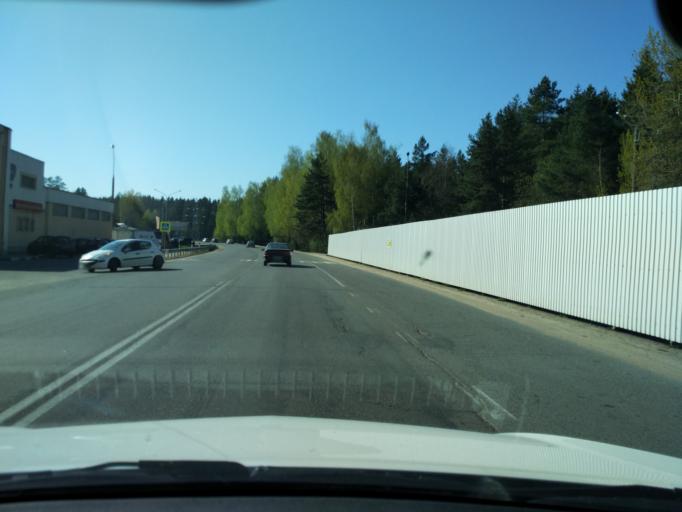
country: BY
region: Minsk
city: Lyeskawka
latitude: 53.9589
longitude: 27.7225
